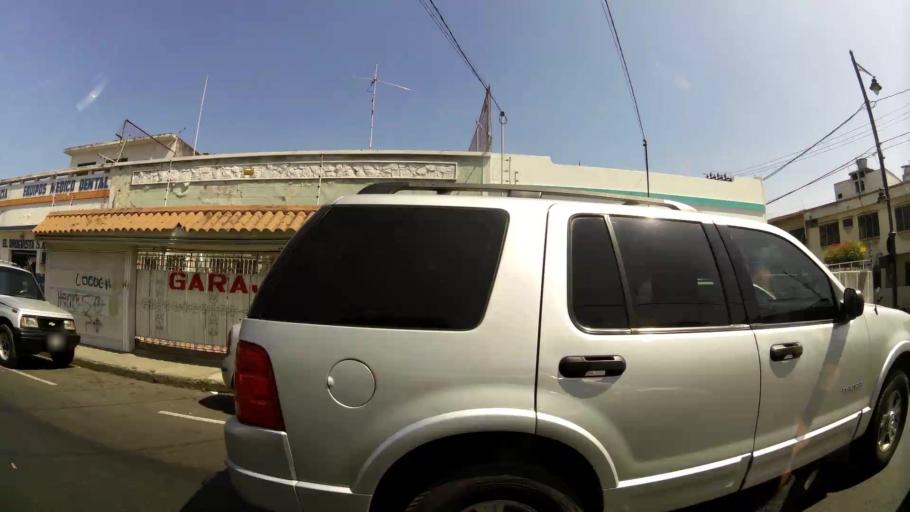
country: EC
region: Guayas
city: Guayaquil
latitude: -2.1854
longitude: -79.8949
